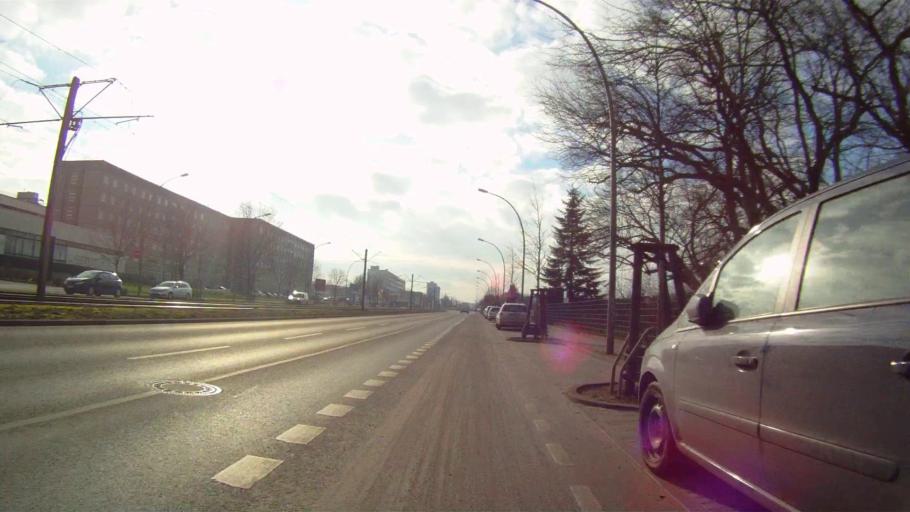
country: DE
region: Berlin
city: Friedrichsfelde
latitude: 52.5213
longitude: 13.5193
